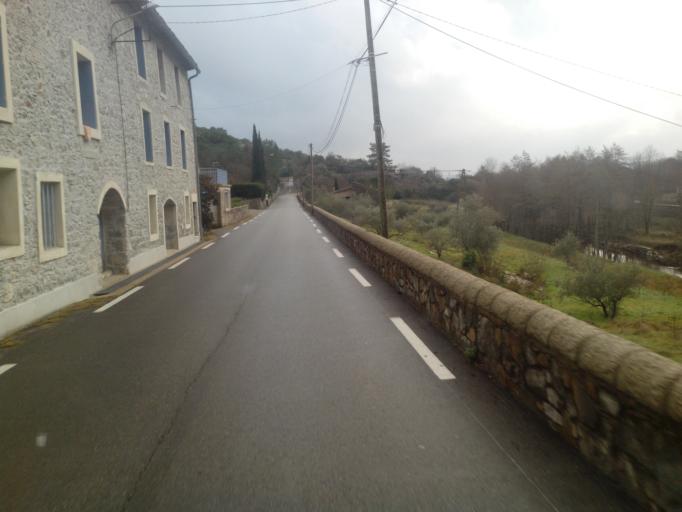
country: FR
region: Languedoc-Roussillon
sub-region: Departement du Gard
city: Saint-Hippolyte-du-Fort
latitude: 43.9721
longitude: 3.8521
